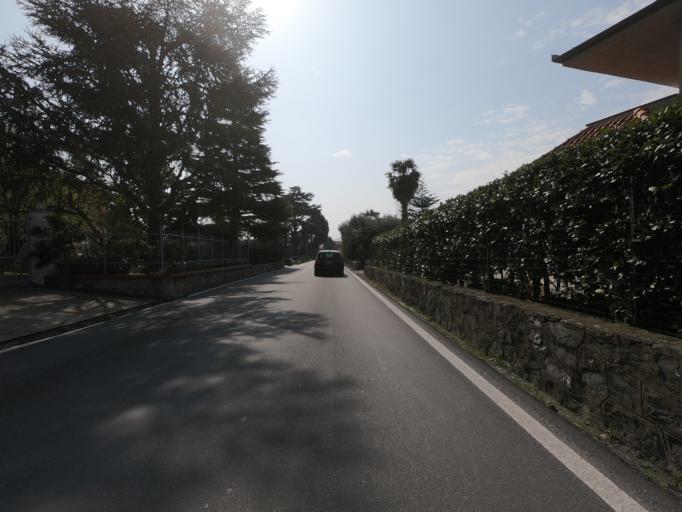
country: IT
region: Liguria
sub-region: Provincia di Savona
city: Cisano
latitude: 44.0864
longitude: 8.1482
